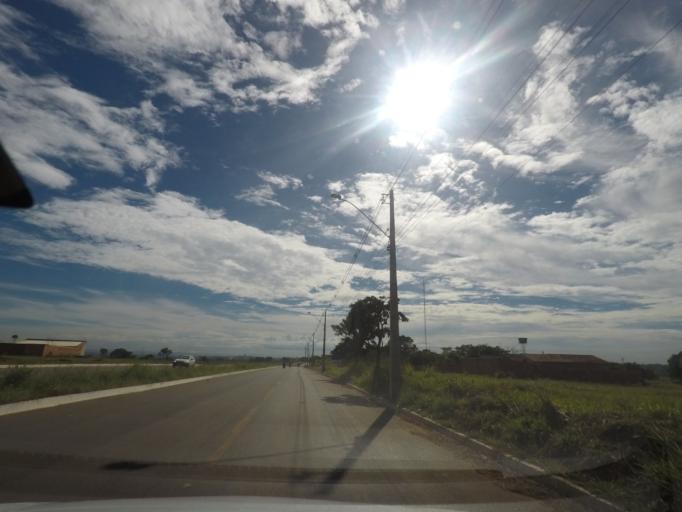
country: BR
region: Goias
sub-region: Aparecida De Goiania
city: Aparecida de Goiania
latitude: -16.8102
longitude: -49.2788
